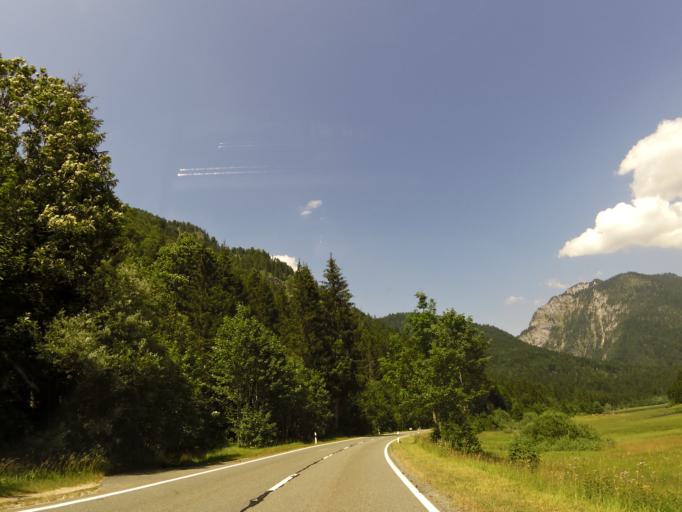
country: DE
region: Bavaria
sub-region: Upper Bavaria
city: Reit im Winkl
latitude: 47.6779
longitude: 12.5459
